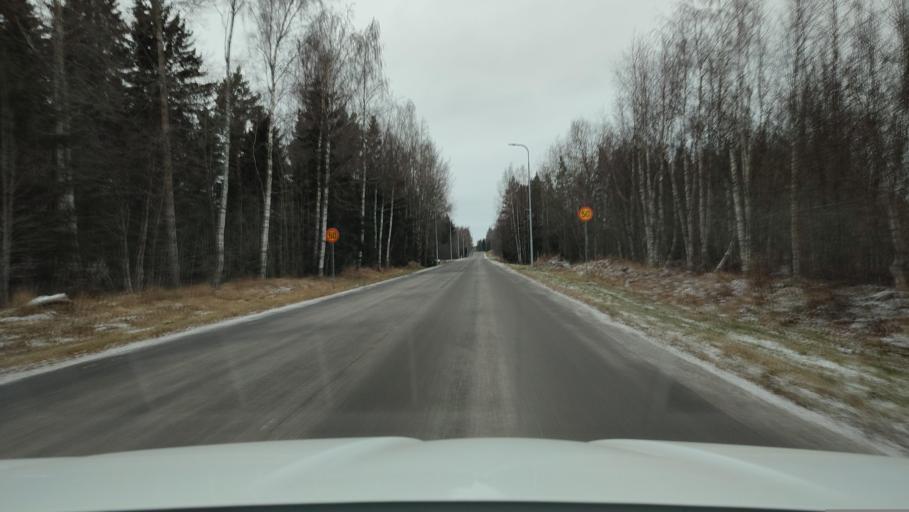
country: FI
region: Ostrobothnia
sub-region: Vaasa
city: Ristinummi
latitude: 63.0407
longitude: 21.7794
